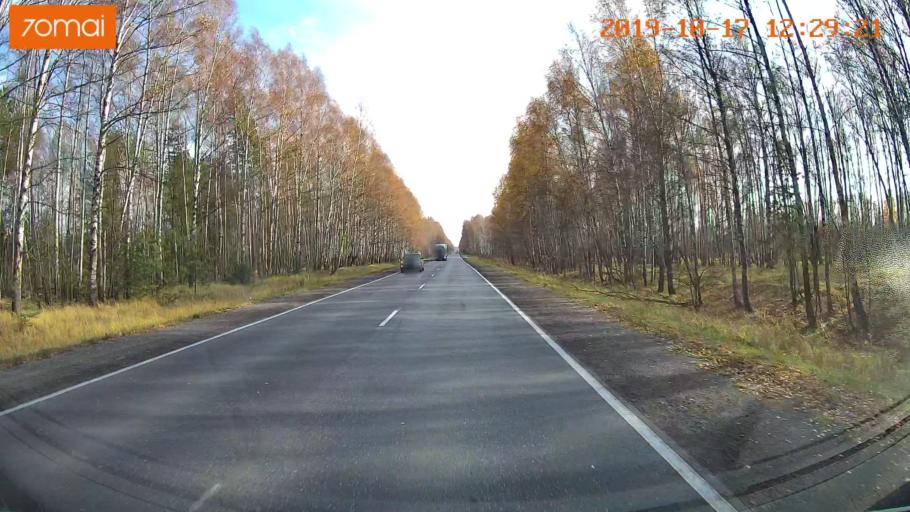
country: RU
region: Rjazan
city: Syntul
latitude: 54.9822
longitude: 41.2901
